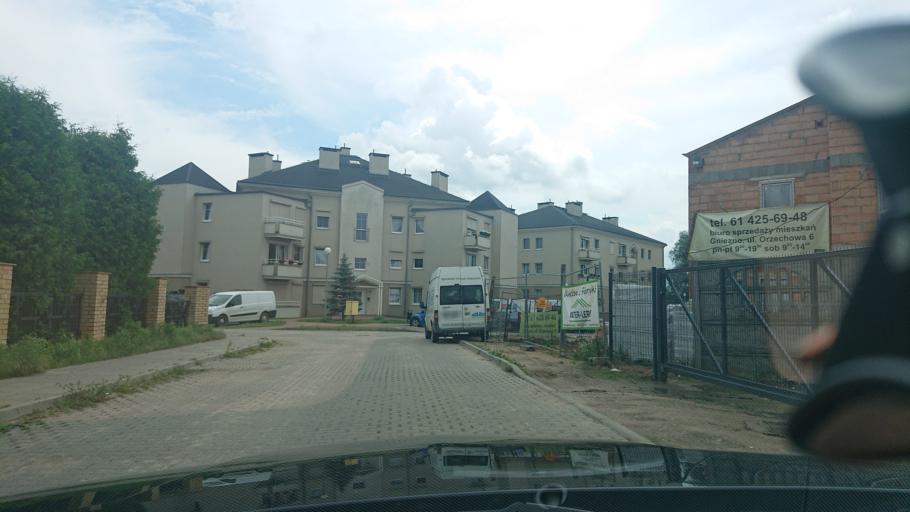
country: PL
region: Greater Poland Voivodeship
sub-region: Powiat gnieznienski
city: Gniezno
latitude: 52.5337
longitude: 17.6294
